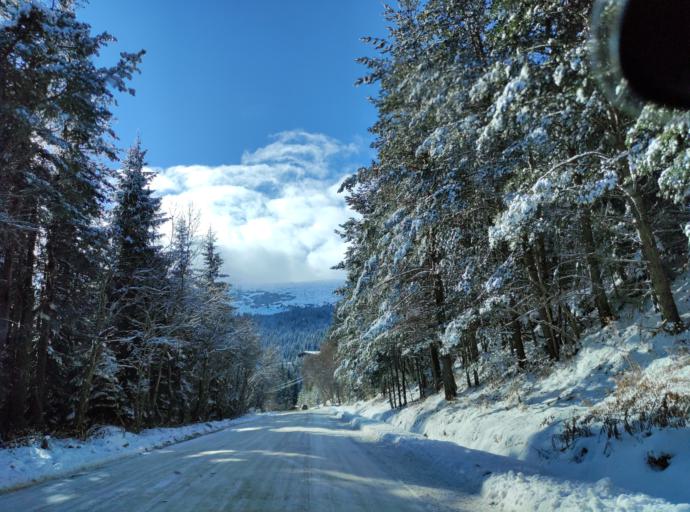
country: BG
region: Sofia-Capital
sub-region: Stolichna Obshtina
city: Sofia
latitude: 42.5905
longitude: 23.2992
